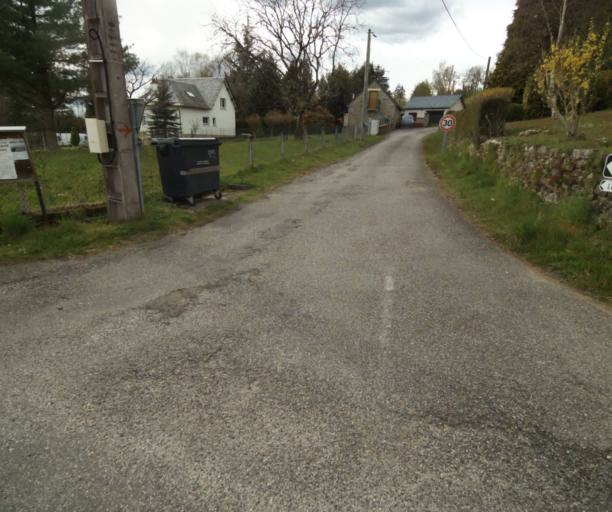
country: FR
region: Limousin
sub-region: Departement de la Correze
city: Argentat
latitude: 45.1898
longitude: 1.9563
